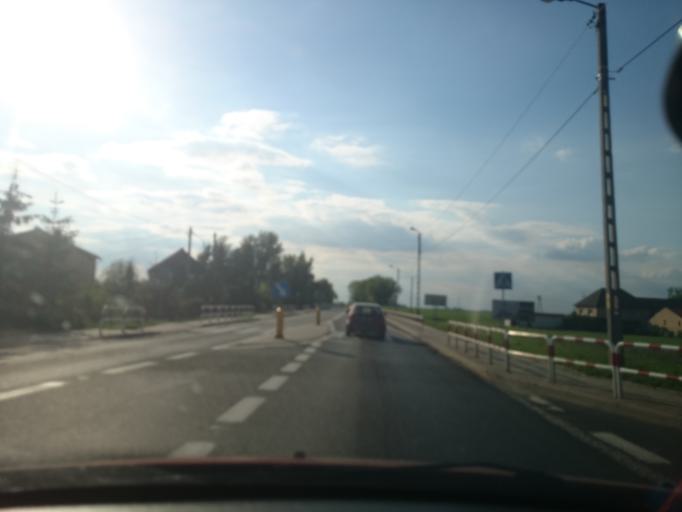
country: PL
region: Opole Voivodeship
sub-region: Powiat strzelecki
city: Izbicko
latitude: 50.5538
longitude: 18.2200
